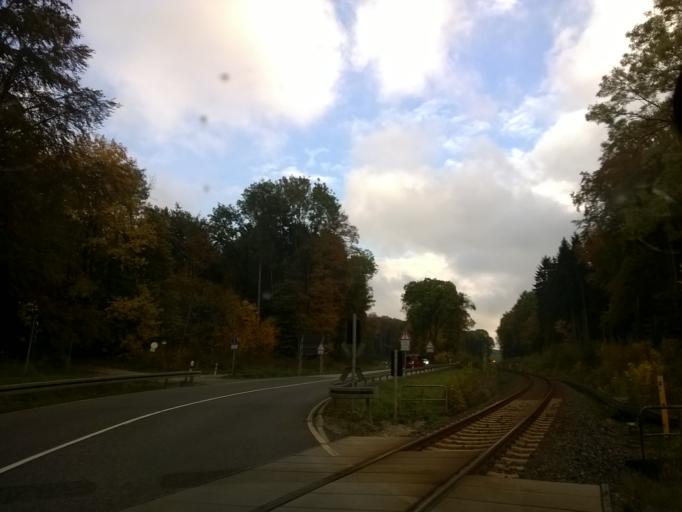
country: DE
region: Thuringia
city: Sondershausen
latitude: 51.3327
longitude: 10.8305
